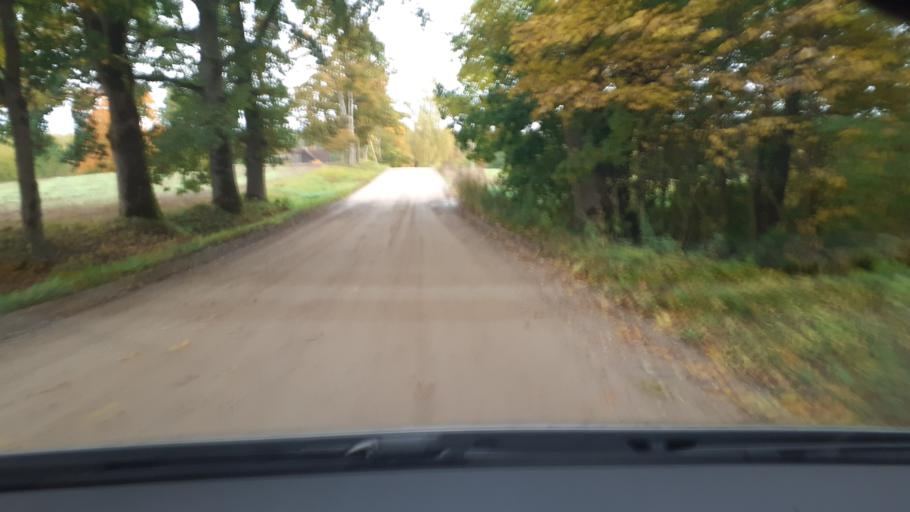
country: LV
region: Kuldigas Rajons
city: Kuldiga
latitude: 57.0249
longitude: 21.9143
